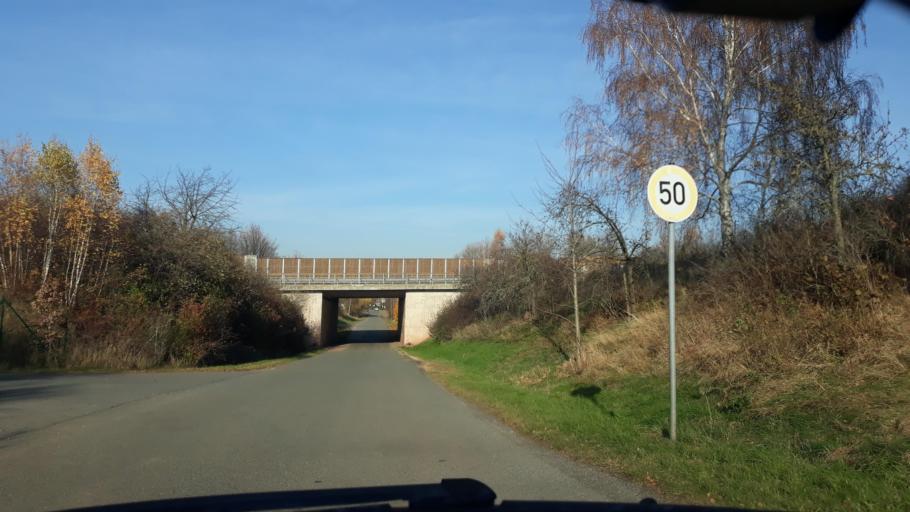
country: DE
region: Saxony
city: Reinsdorf
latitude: 50.6744
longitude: 12.5626
